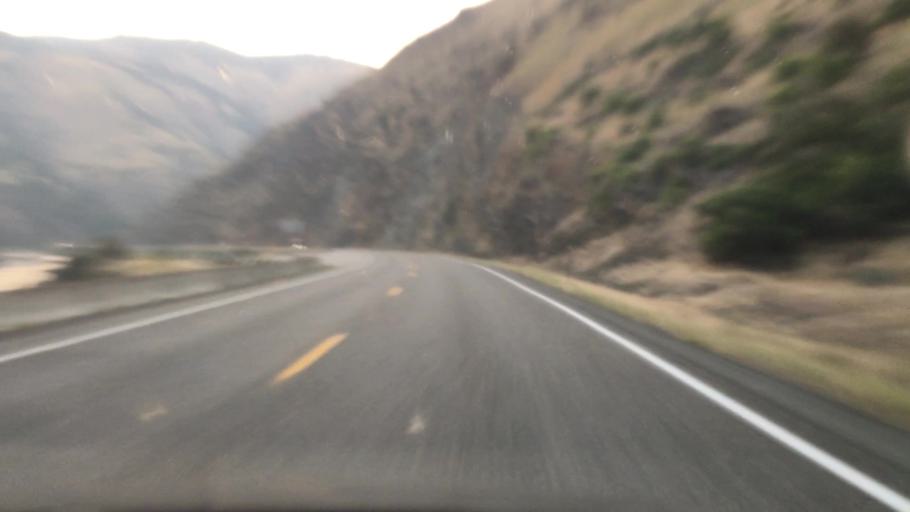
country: US
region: Idaho
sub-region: Idaho County
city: Grangeville
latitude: 45.6188
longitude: -116.2880
